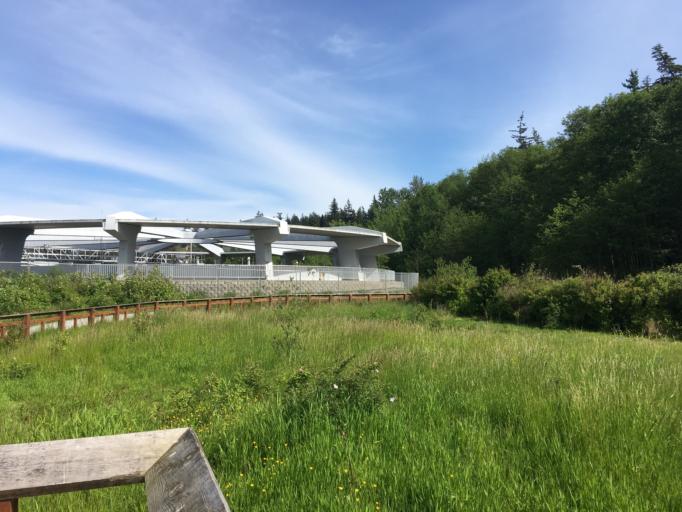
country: US
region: Washington
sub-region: Whatcom County
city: Bellingham
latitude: 48.7176
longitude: -122.5159
